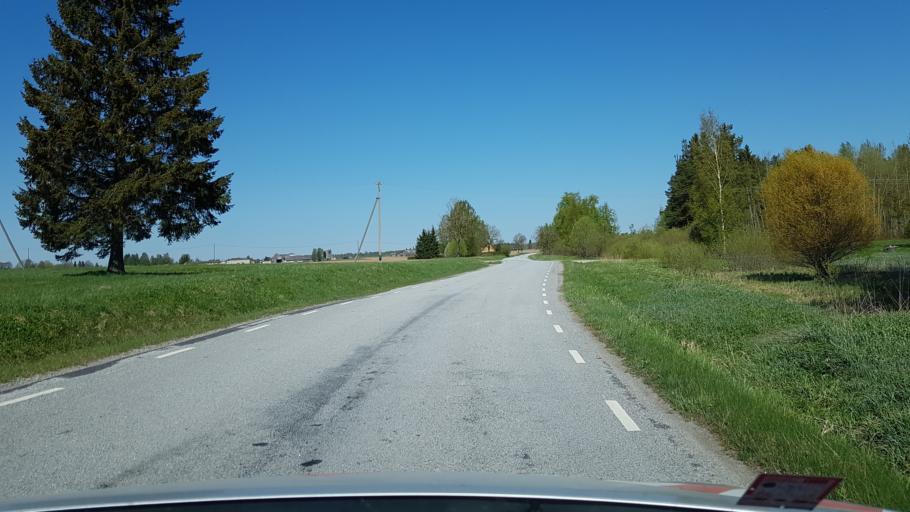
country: EE
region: Vorumaa
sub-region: Voru linn
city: Voru
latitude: 57.9113
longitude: 26.9584
